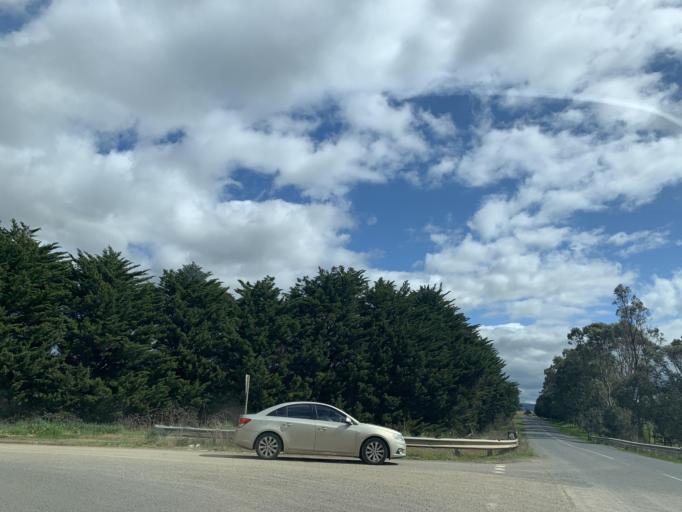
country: AU
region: Victoria
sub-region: Whittlesea
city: Whittlesea
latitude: -37.2792
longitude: 144.9305
